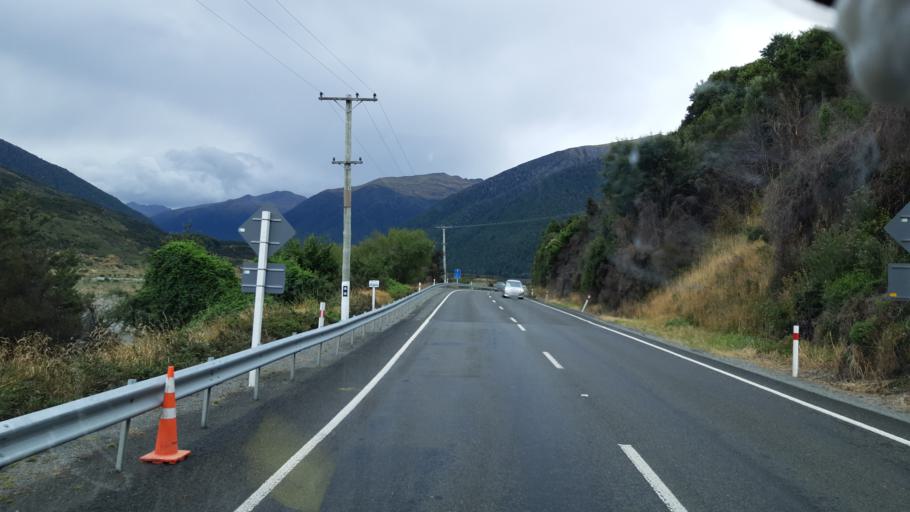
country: NZ
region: Canterbury
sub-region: Hurunui District
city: Amberley
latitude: -42.5623
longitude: 172.3532
